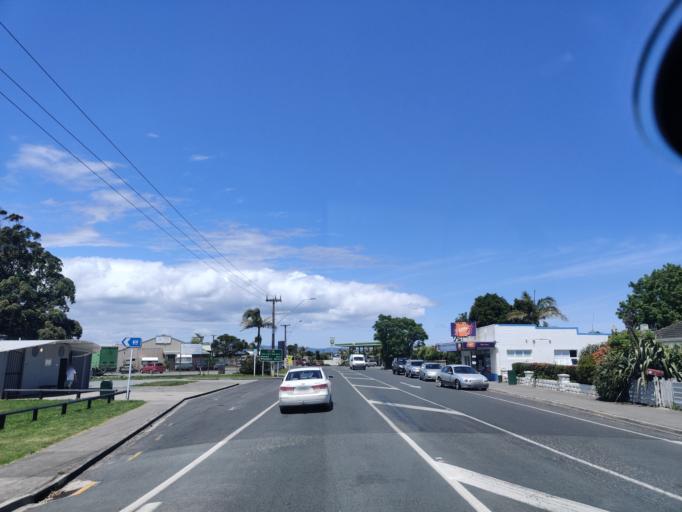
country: NZ
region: Northland
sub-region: Far North District
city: Kaitaia
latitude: -35.0465
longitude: 173.2564
